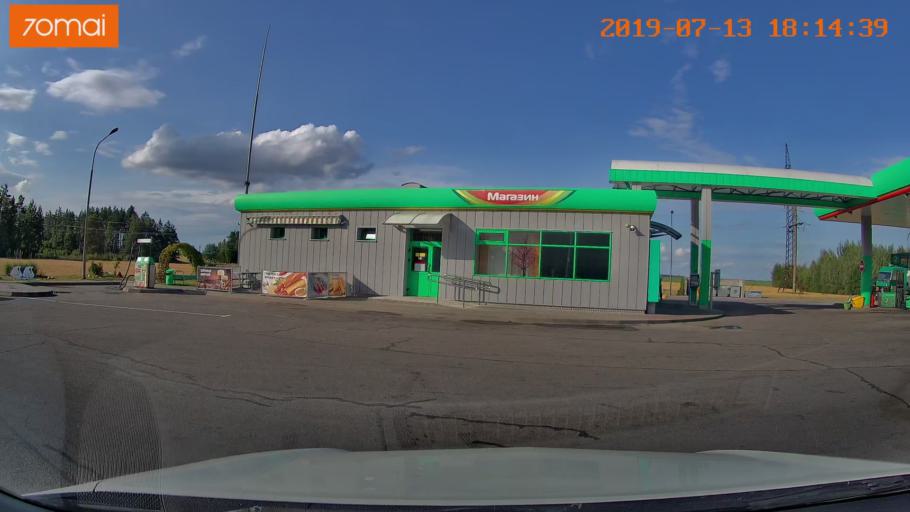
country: BY
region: Minsk
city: Dukora
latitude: 53.6202
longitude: 28.0506
